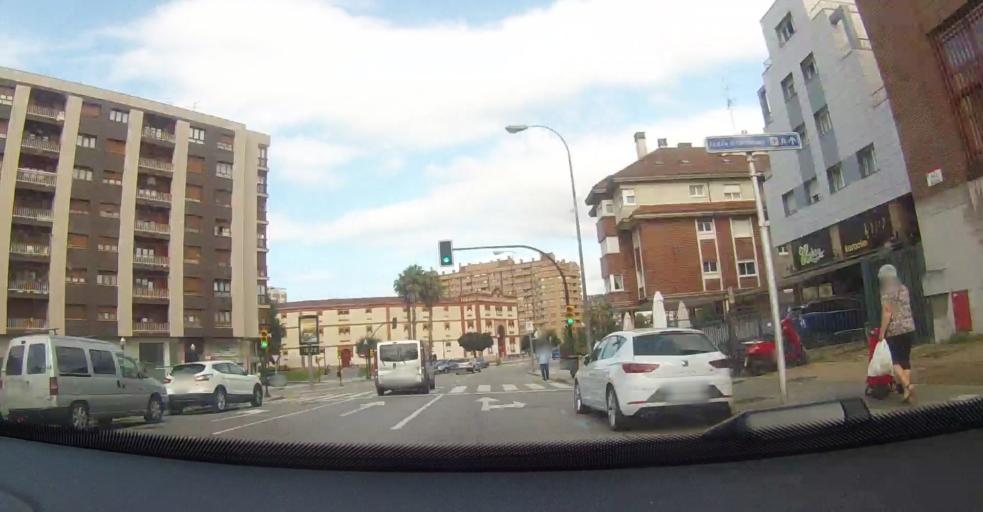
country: ES
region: Asturias
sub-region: Province of Asturias
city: Gijon
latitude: 43.5353
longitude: -5.6473
